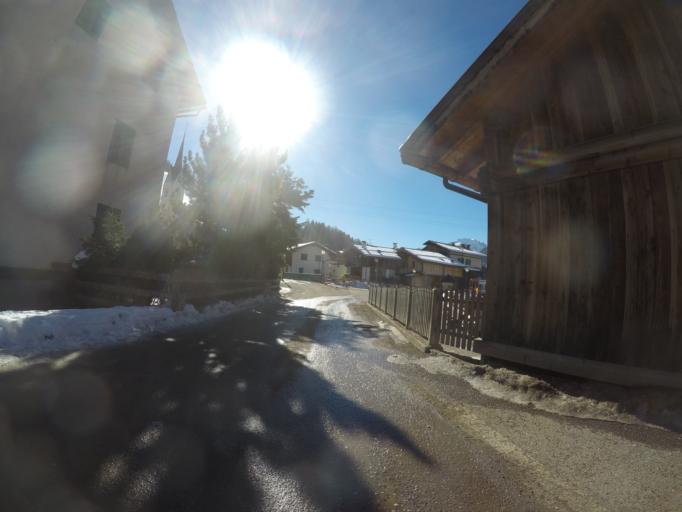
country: IT
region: Trentino-Alto Adige
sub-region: Provincia di Trento
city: Pozza di Fassa
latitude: 46.4303
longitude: 11.6947
